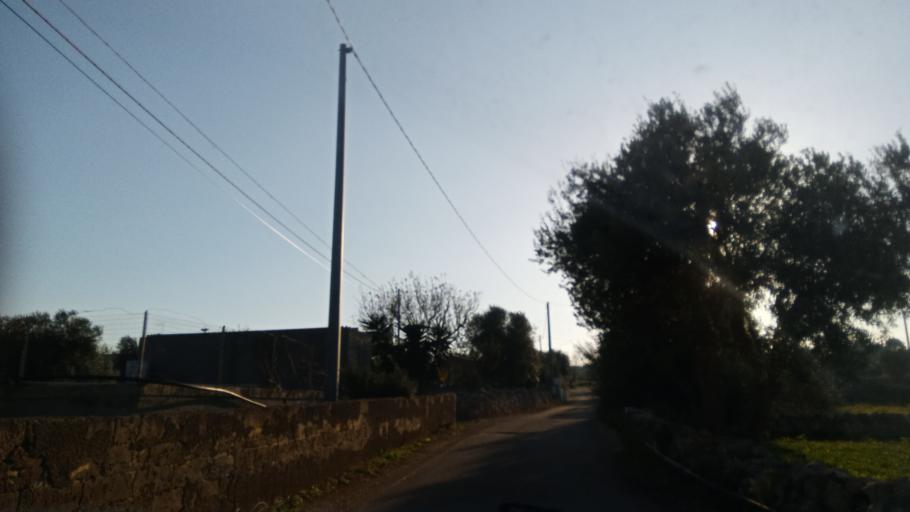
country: IT
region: Apulia
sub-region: Provincia di Bari
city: Polignano a Mare
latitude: 40.9813
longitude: 17.2083
